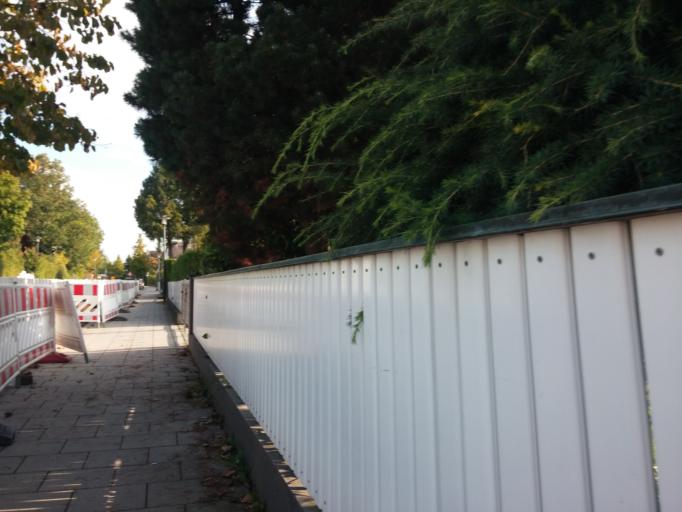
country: DE
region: Bavaria
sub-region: Upper Bavaria
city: Feldkirchen
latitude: 48.1466
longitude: 11.7347
